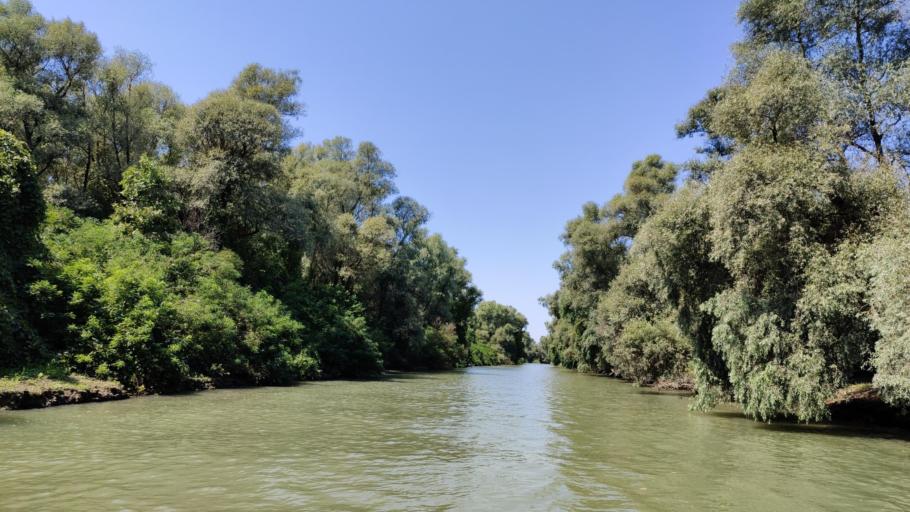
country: RO
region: Tulcea
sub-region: Comuna Pardina
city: Pardina
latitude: 45.2542
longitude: 28.9463
